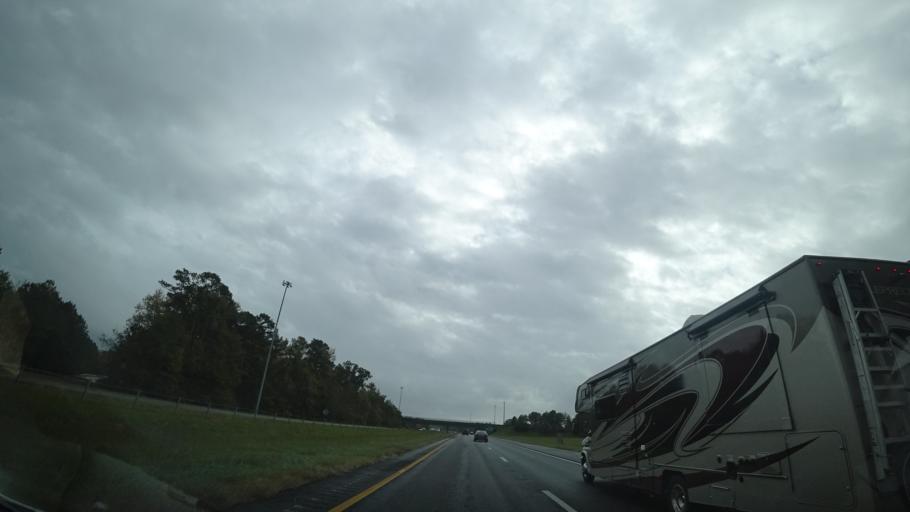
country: US
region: Virginia
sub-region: City of Portsmouth
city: Portsmouth Heights
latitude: 36.8066
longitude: -76.4305
